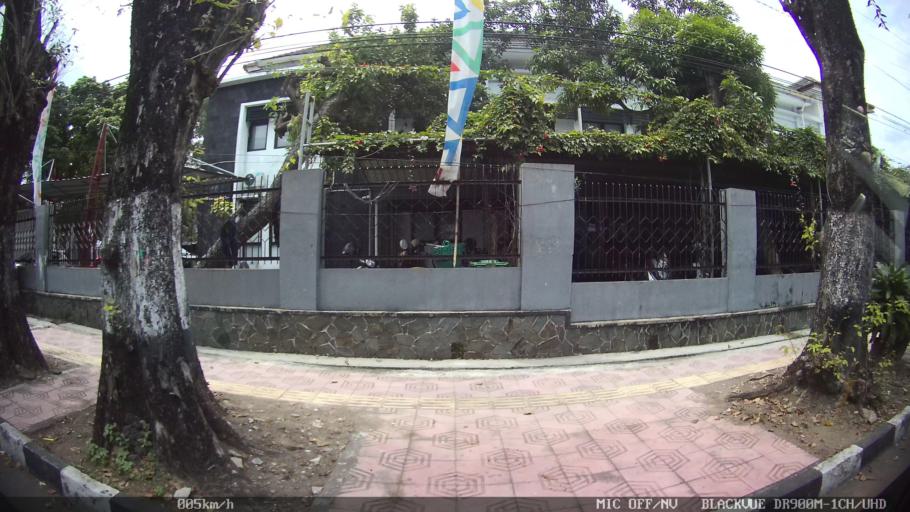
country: ID
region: Daerah Istimewa Yogyakarta
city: Yogyakarta
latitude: -7.7976
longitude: 110.3817
